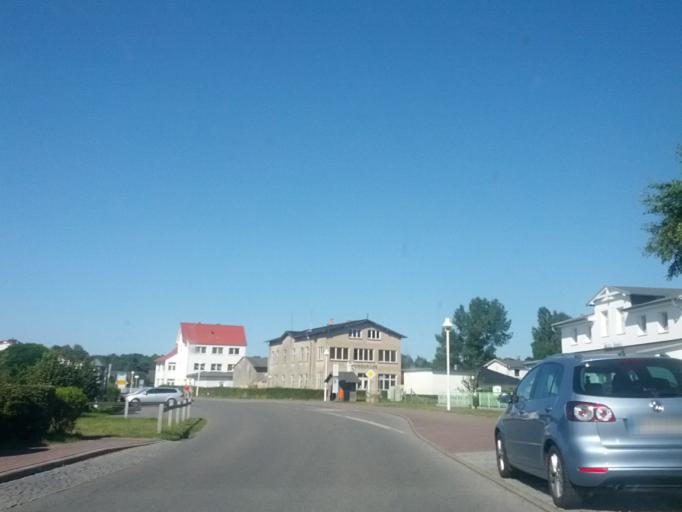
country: DE
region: Mecklenburg-Vorpommern
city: Ostseebad Gohren
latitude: 54.2753
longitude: 13.7146
